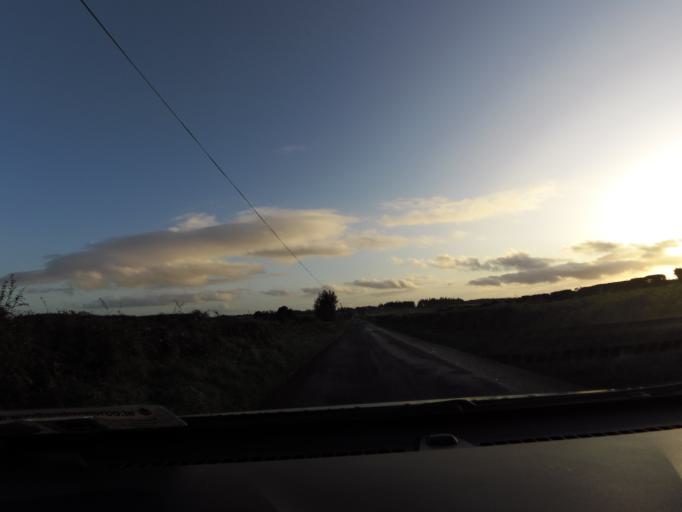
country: IE
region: Connaught
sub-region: Roscommon
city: Castlerea
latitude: 53.6491
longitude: -8.6048
